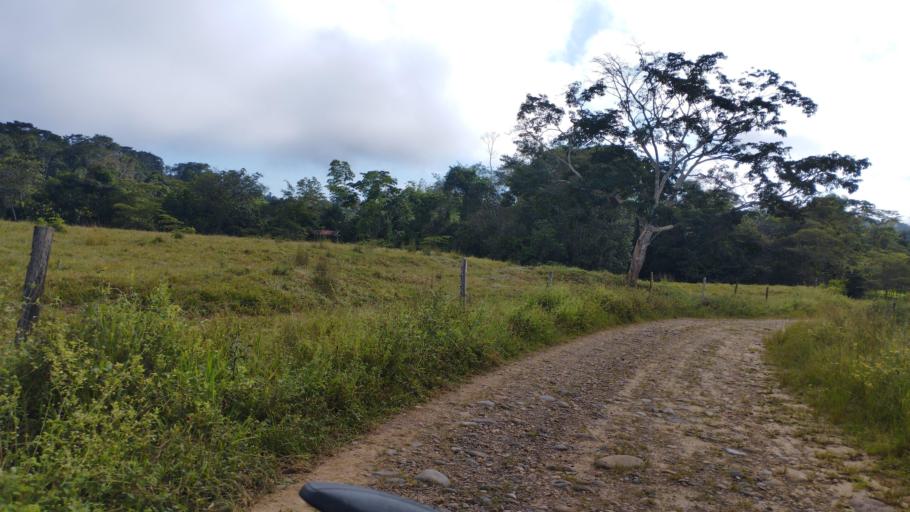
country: CO
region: Casanare
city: Sabanalarga
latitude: 4.7592
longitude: -73.0737
